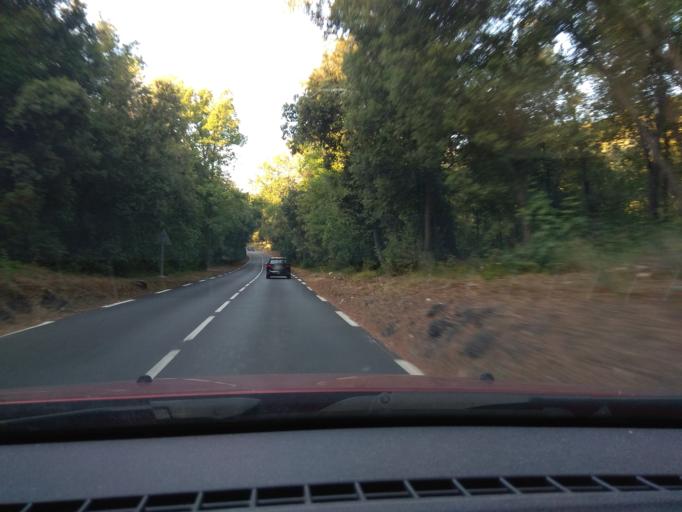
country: FR
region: Provence-Alpes-Cote d'Azur
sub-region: Departement des Alpes-Maritimes
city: Le Rouret
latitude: 43.6586
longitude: 7.0287
